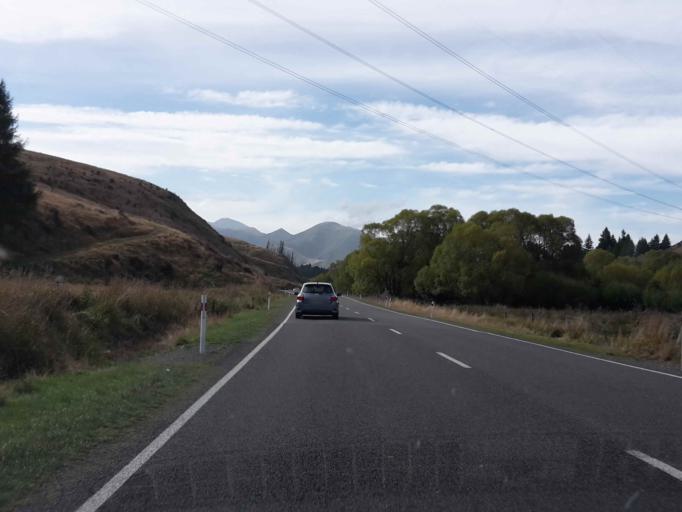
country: NZ
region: Canterbury
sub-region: Timaru District
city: Pleasant Point
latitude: -44.0677
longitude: 170.6710
